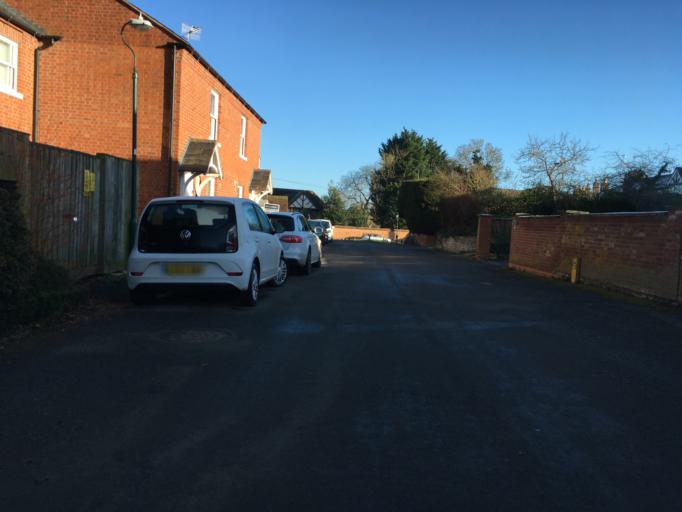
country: GB
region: England
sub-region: Warwickshire
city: Stratford-upon-Avon
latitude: 52.2061
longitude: -1.6574
